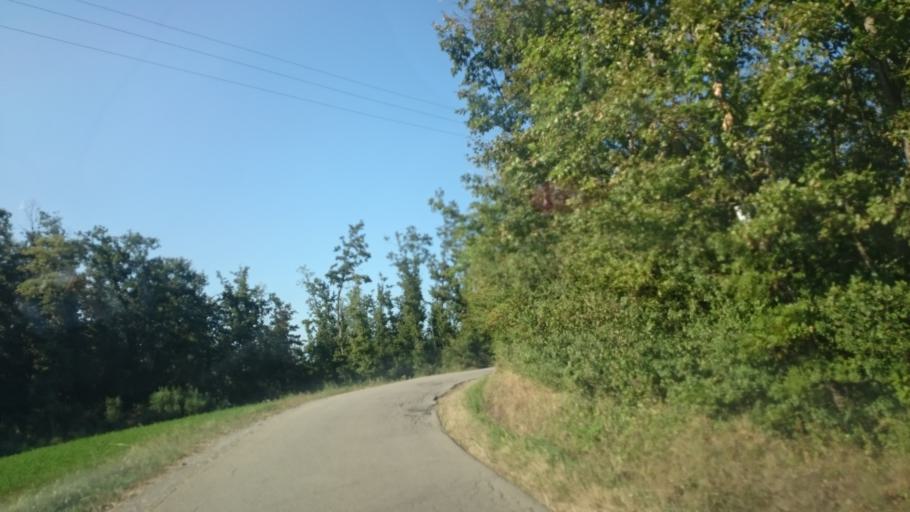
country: IT
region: Emilia-Romagna
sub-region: Provincia di Reggio Emilia
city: Villa Minozzo
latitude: 44.3408
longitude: 10.4791
